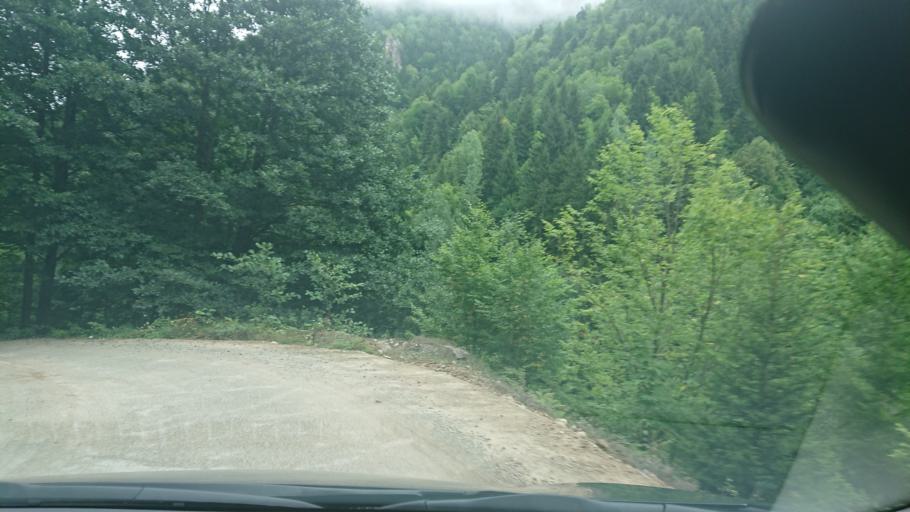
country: TR
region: Gumushane
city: Kurtun
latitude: 40.6786
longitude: 39.0481
